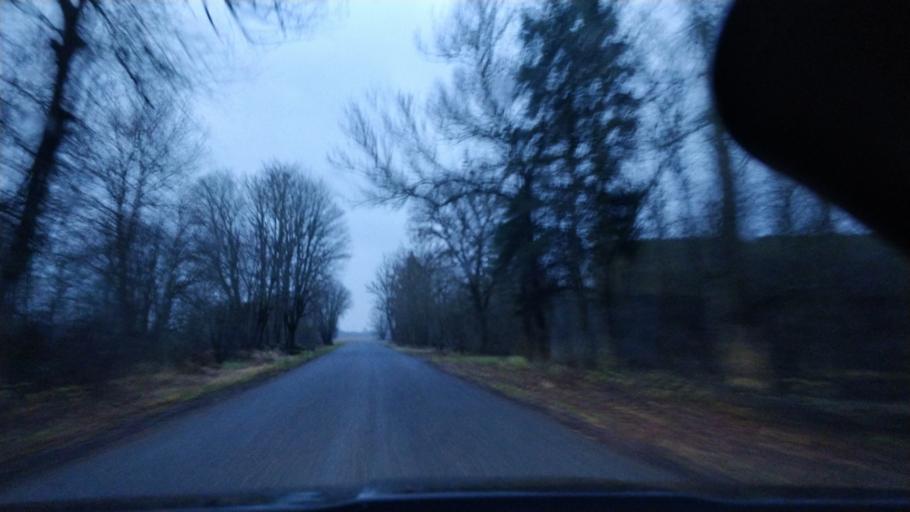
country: EE
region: Laeaene
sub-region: Lihula vald
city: Lihula
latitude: 58.8533
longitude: 24.0139
